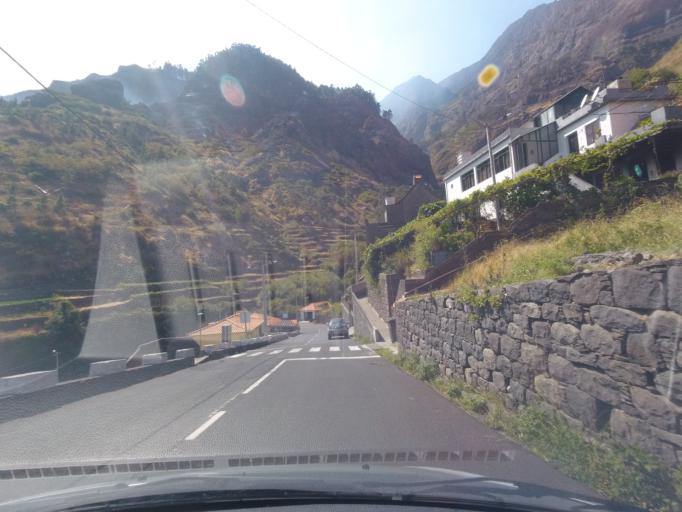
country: PT
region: Madeira
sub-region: Camara de Lobos
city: Curral das Freiras
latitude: 32.7303
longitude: -17.0280
